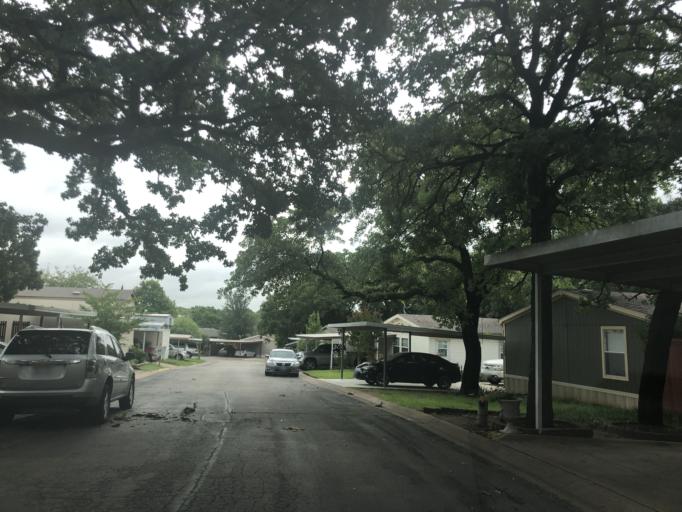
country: US
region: Texas
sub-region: Dallas County
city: Irving
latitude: 32.8072
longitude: -96.9967
